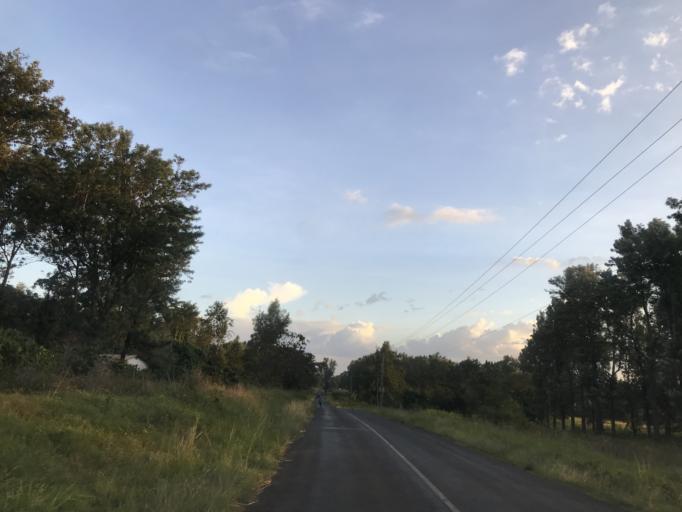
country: TZ
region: Arusha
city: Usa River
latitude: -3.3539
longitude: 36.8646
